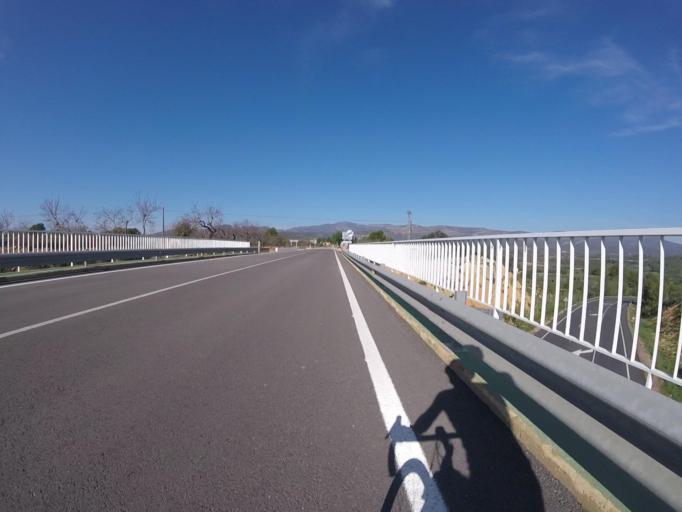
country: ES
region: Valencia
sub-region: Provincia de Castello
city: Cuevas de Vinroma
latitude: 40.2603
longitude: 0.0780
